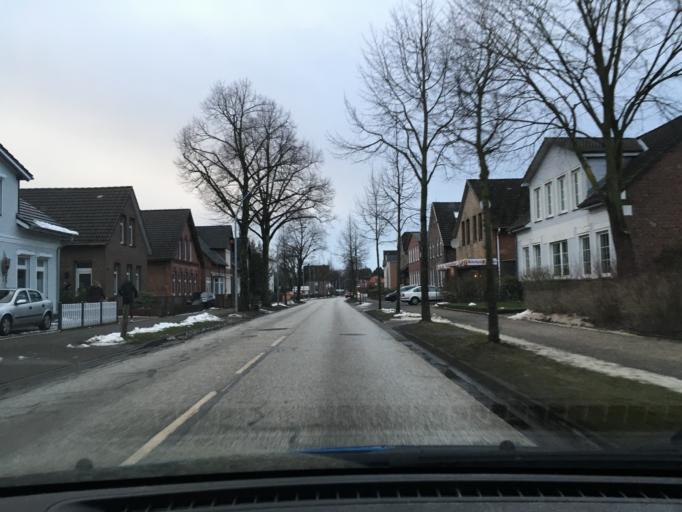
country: DE
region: Schleswig-Holstein
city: Itzehoe
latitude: 53.9334
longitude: 9.5035
